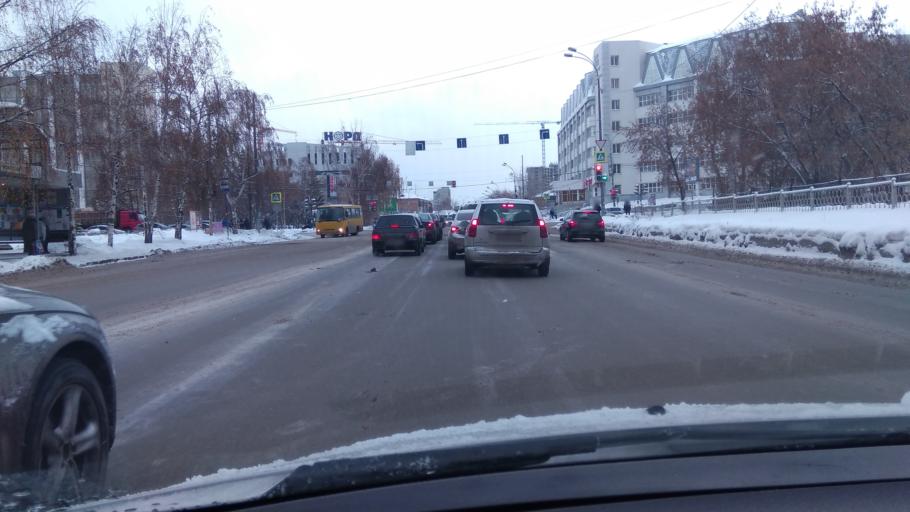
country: RU
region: Sverdlovsk
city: Sovkhoznyy
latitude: 56.8188
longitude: 60.5588
